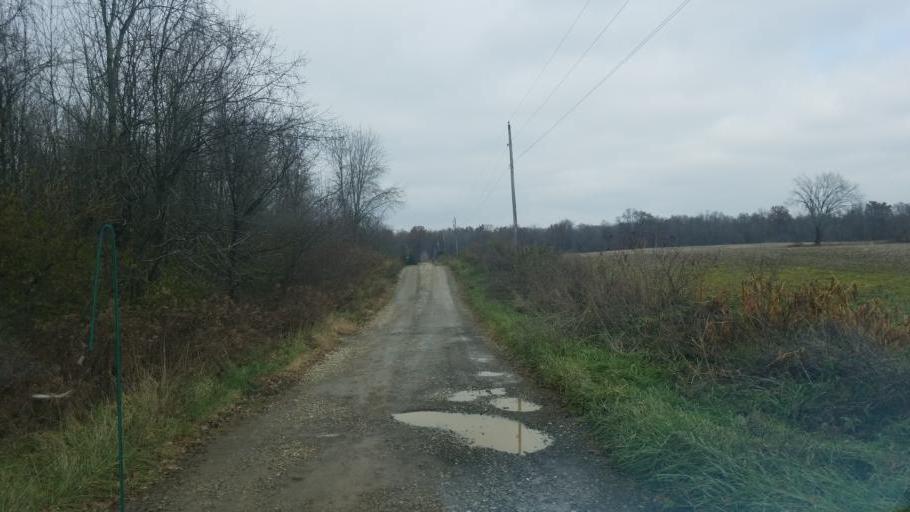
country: US
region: Ohio
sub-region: Morrow County
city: Cardington
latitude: 40.4389
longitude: -82.8395
